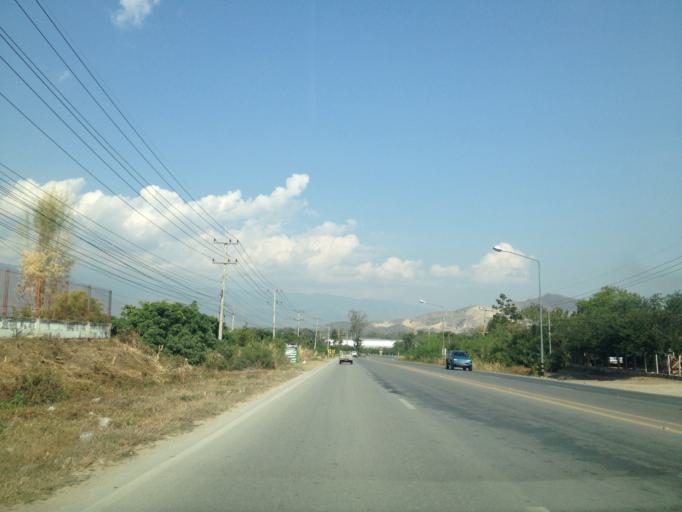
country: TH
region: Chiang Mai
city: Hot
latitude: 18.2151
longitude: 98.6152
